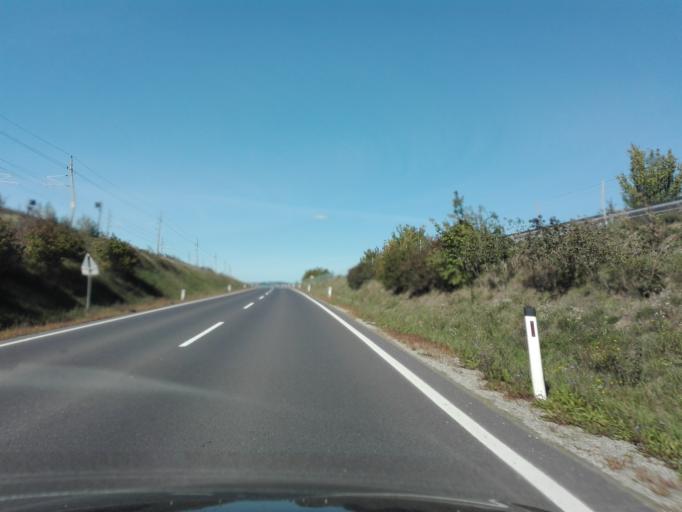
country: AT
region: Lower Austria
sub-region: Politischer Bezirk Amstetten
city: Ennsdorf
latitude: 48.2089
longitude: 14.5088
